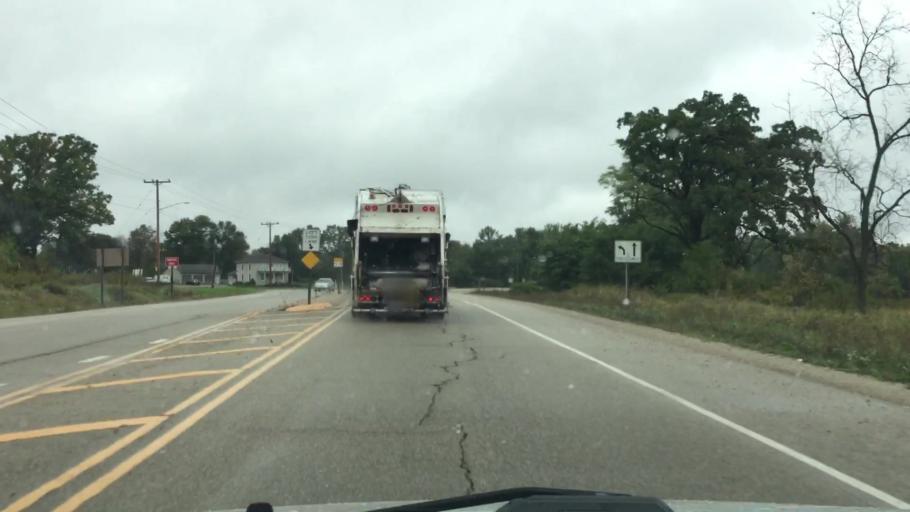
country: US
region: Wisconsin
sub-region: Walworth County
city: Whitewater
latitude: 42.8214
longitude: -88.7455
